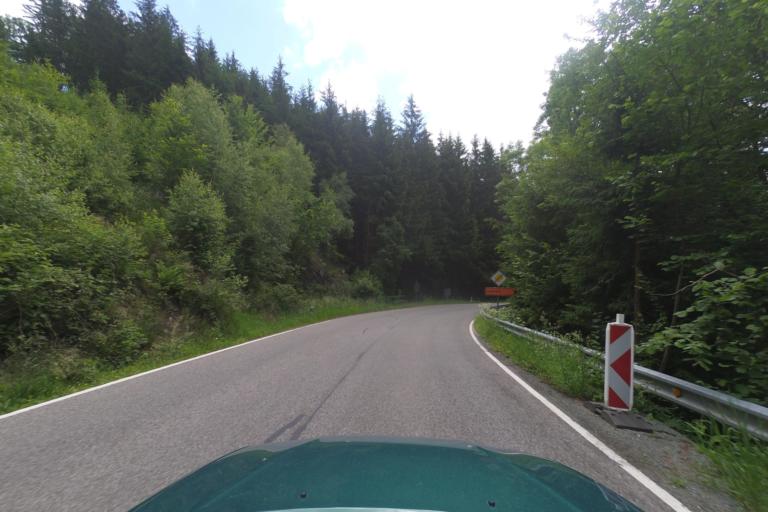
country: PL
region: Lower Silesian Voivodeship
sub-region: Powiat klodzki
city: Lewin Klodzki
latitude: 50.3491
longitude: 16.2403
